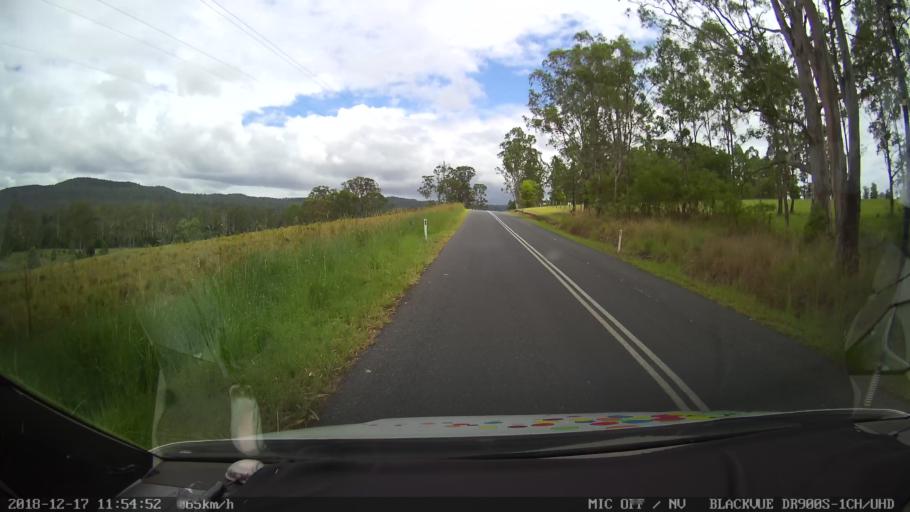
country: AU
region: New South Wales
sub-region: Kyogle
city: Kyogle
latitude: -28.5619
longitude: 152.5815
